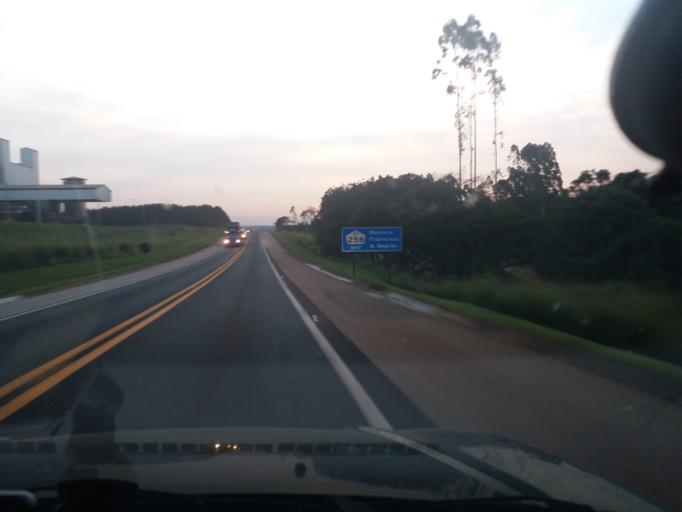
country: BR
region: Sao Paulo
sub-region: Buri
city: Buri
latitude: -23.9381
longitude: -48.6184
